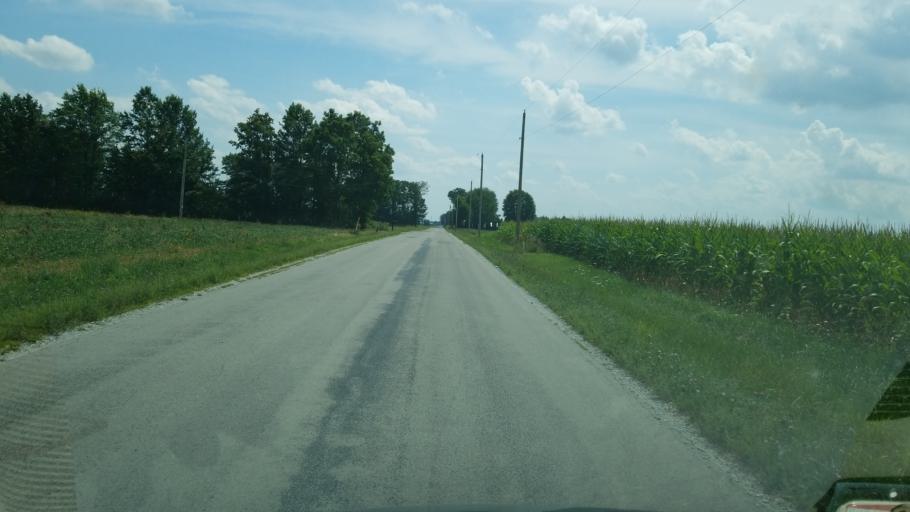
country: US
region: Ohio
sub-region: Wyandot County
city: Carey
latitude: 40.8987
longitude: -83.4623
